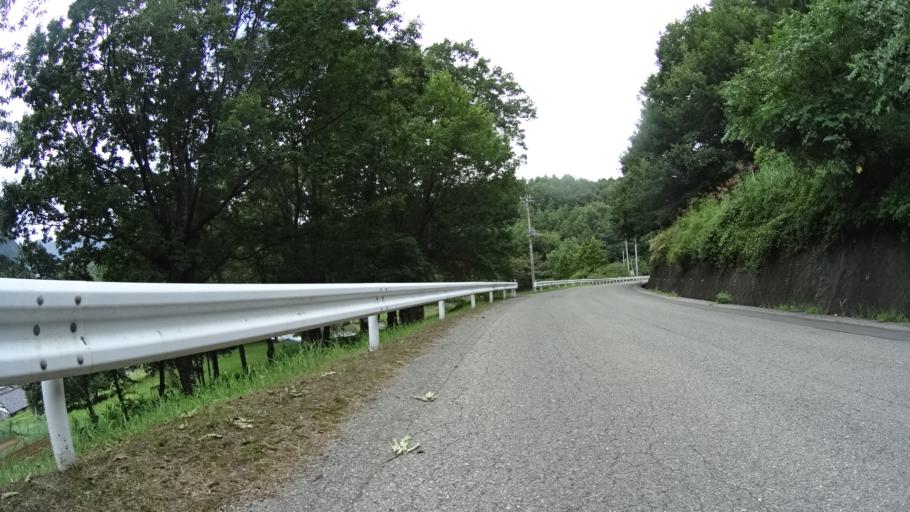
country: JP
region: Yamanashi
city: Nirasaki
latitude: 35.8579
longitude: 138.5213
